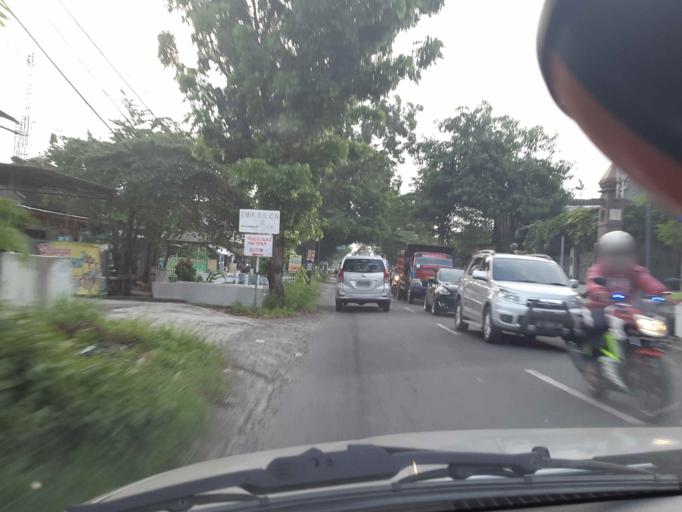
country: ID
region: Central Java
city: Jaten
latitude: -7.5327
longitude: 110.9021
